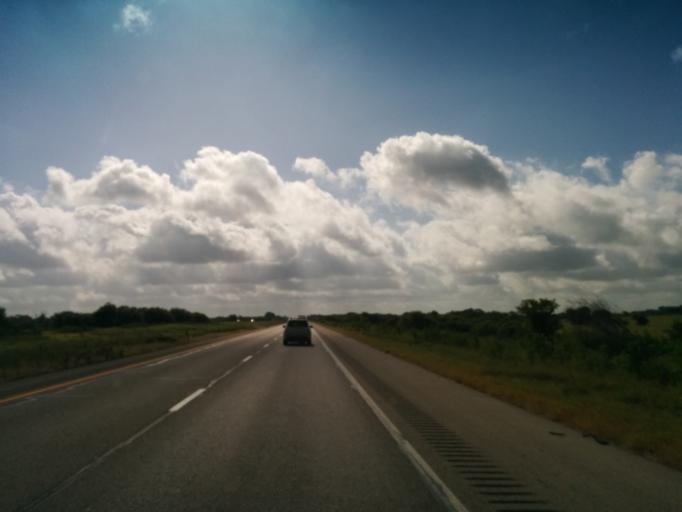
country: US
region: Texas
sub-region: Caldwell County
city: Luling
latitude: 29.6501
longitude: -97.6468
